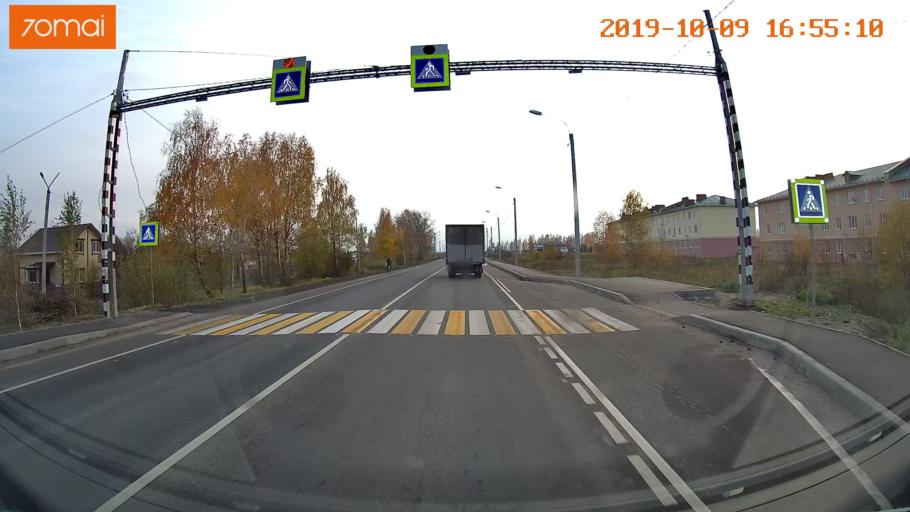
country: RU
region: Ivanovo
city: Privolzhsk
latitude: 57.3695
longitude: 41.2757
